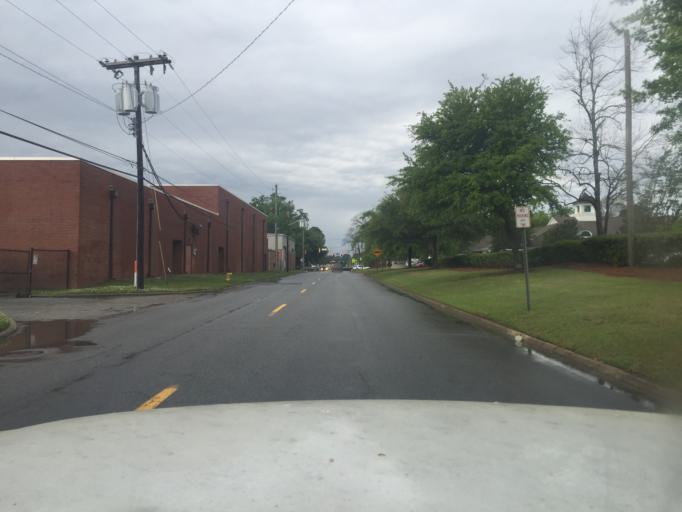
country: US
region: Georgia
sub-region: Chatham County
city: Thunderbolt
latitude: 32.0341
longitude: -81.0947
